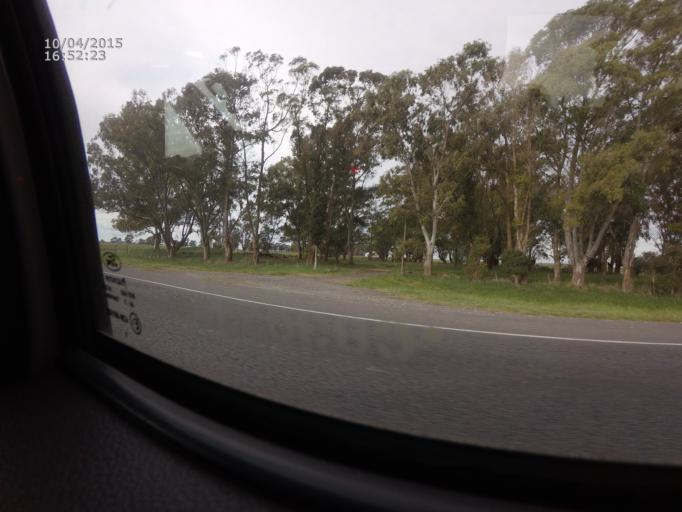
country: AR
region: Buenos Aires
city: Coronel Vidal
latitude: -37.5954
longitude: -57.6879
